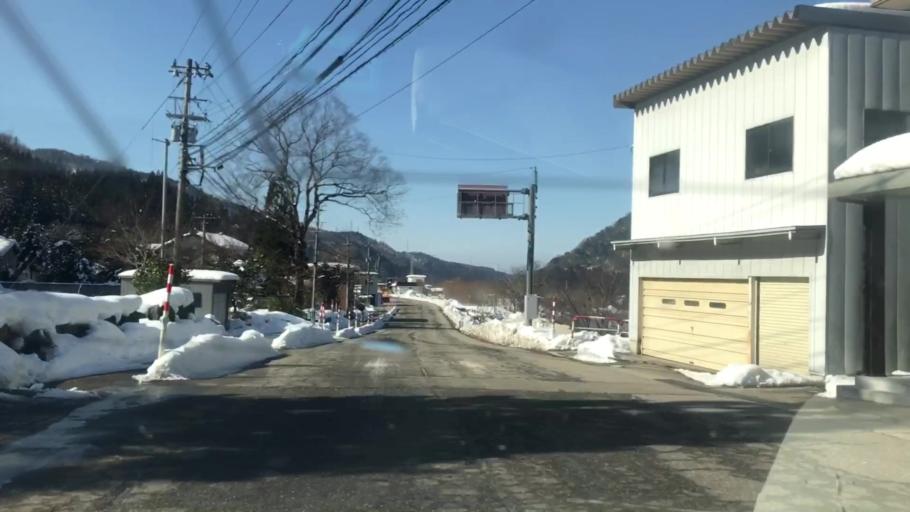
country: JP
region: Toyama
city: Kamiichi
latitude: 36.5694
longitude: 137.3612
